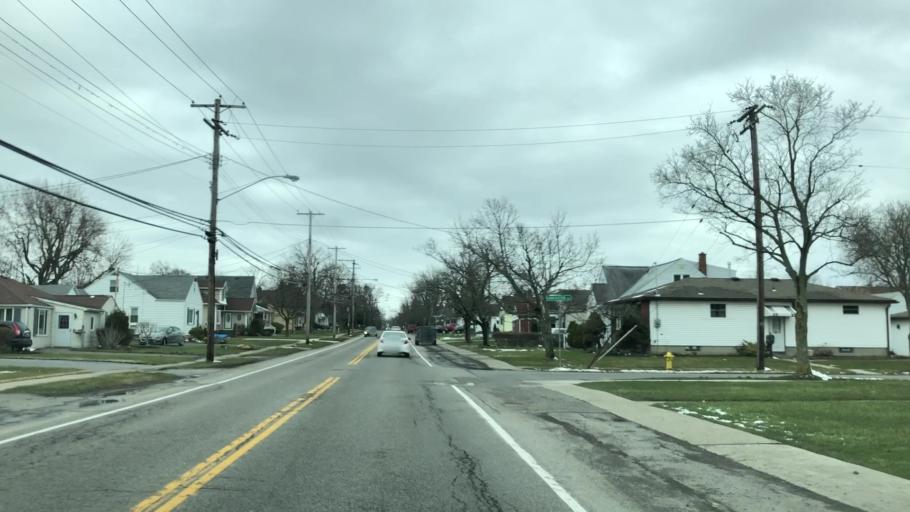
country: US
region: New York
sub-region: Erie County
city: Lancaster
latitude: 42.8902
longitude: -78.6766
